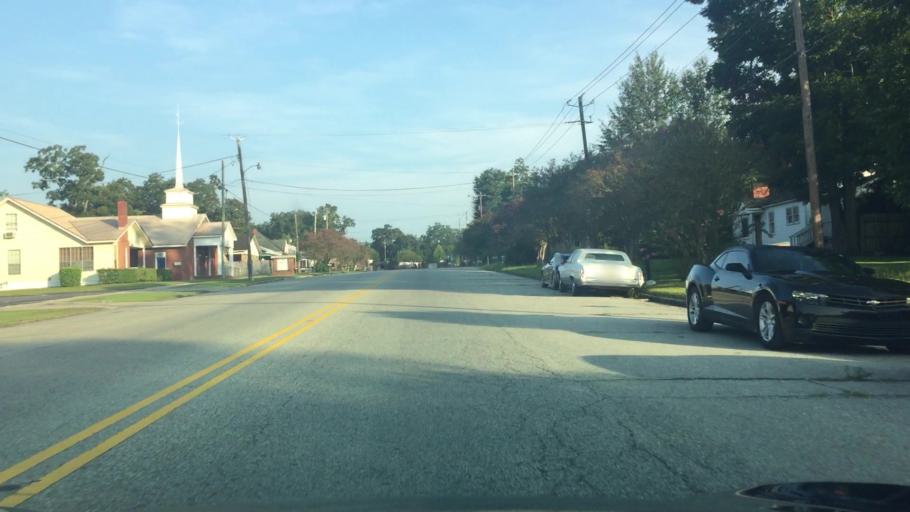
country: US
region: Alabama
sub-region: Covington County
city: Florala
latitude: 31.0075
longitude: -86.3316
